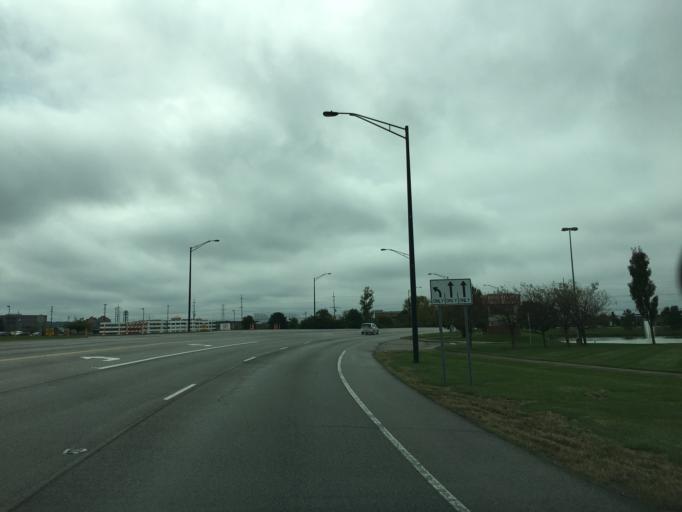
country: US
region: Ohio
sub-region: Butler County
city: Beckett Ridge
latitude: 39.3320
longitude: -84.4355
